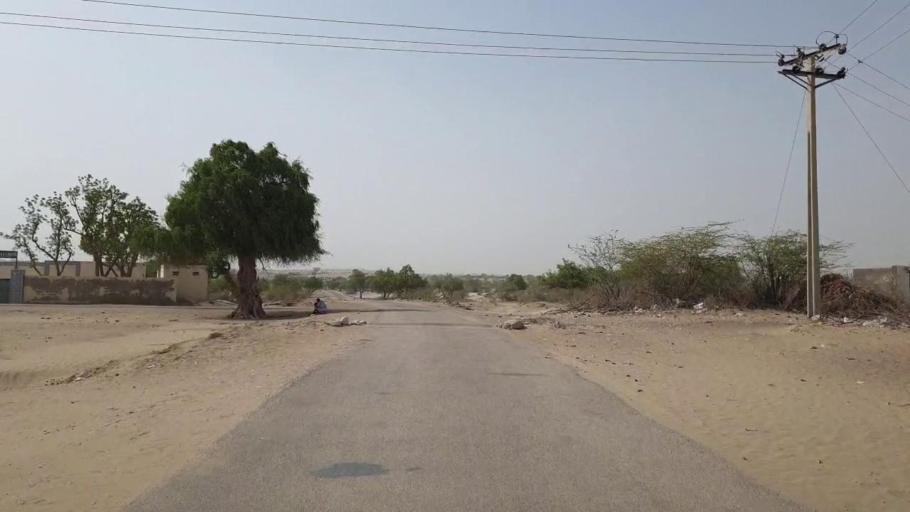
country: PK
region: Sindh
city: Mithi
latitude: 24.6136
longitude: 69.9200
